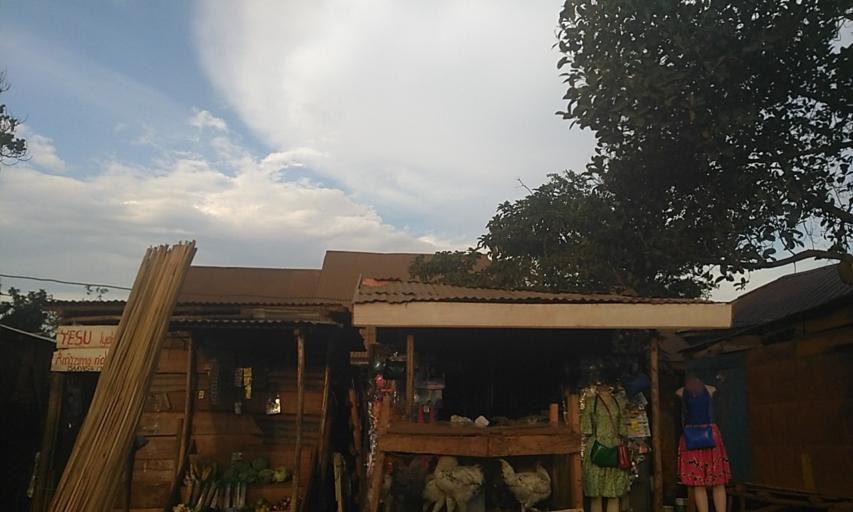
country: UG
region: Central Region
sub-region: Wakiso District
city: Kajansi
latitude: 0.2530
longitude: 32.5356
